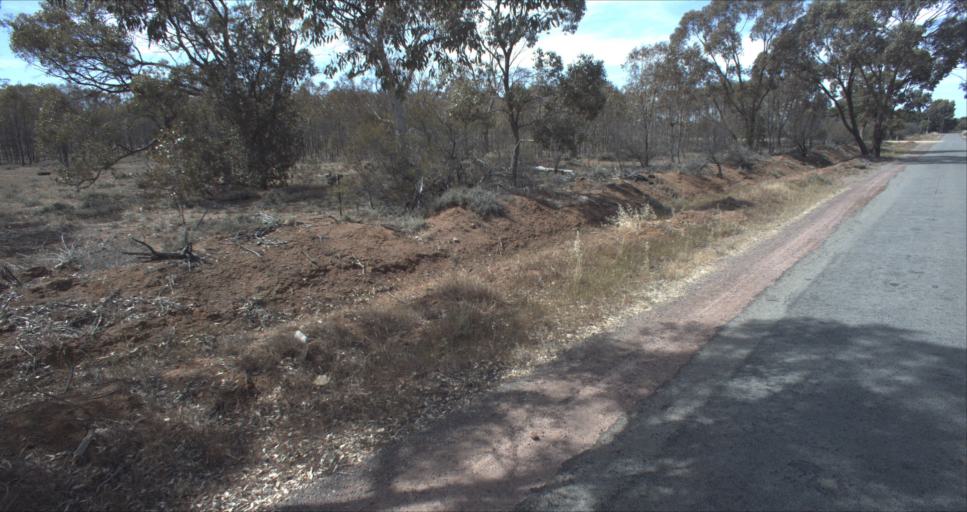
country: AU
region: New South Wales
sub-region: Leeton
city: Leeton
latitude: -34.5665
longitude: 146.4561
